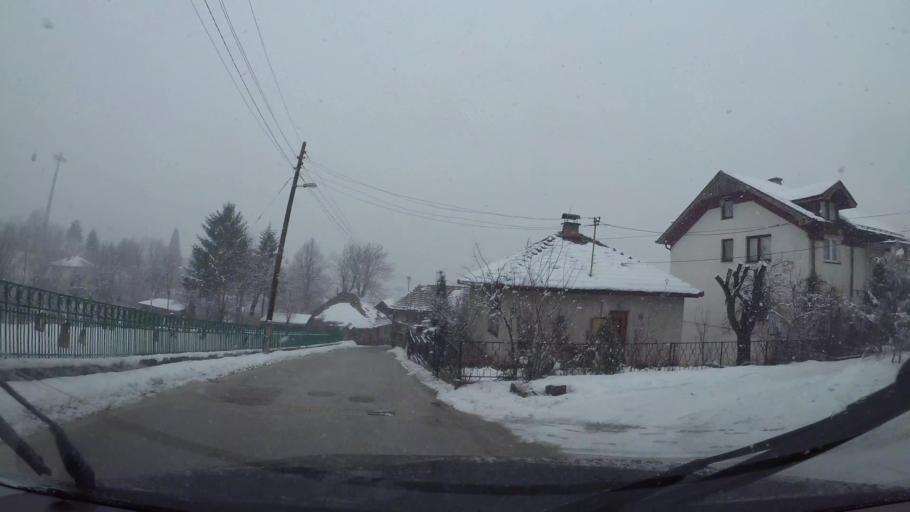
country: BA
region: Federation of Bosnia and Herzegovina
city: Kobilja Glava
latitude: 43.8534
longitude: 18.4399
